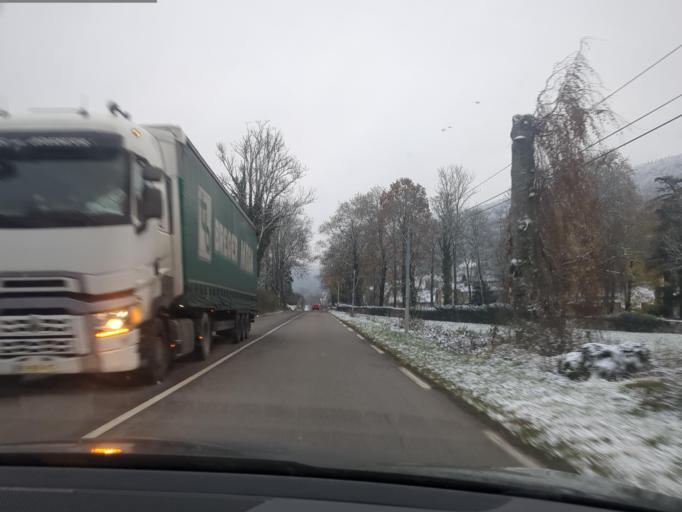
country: FR
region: Franche-Comte
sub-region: Departement du Jura
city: Perrigny
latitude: 46.6397
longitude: 5.6024
